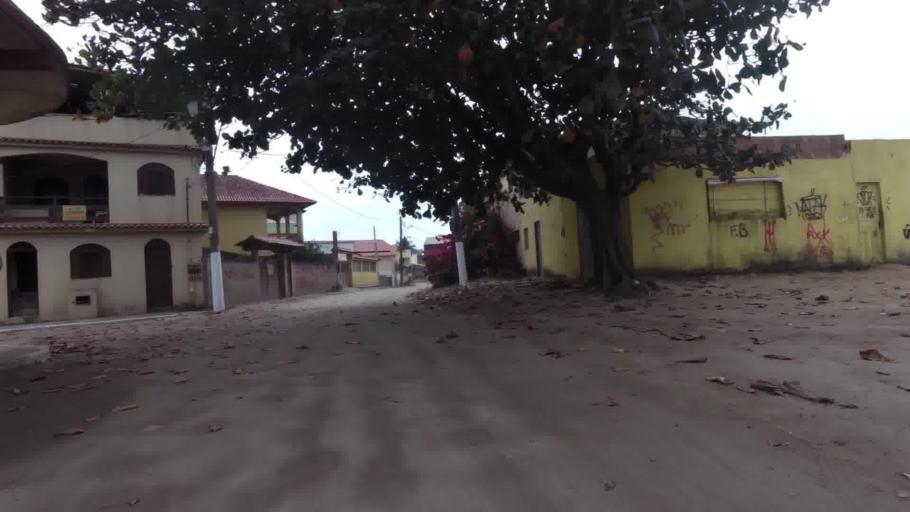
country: BR
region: Espirito Santo
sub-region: Marataizes
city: Marataizes
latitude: -21.0385
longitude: -40.8190
